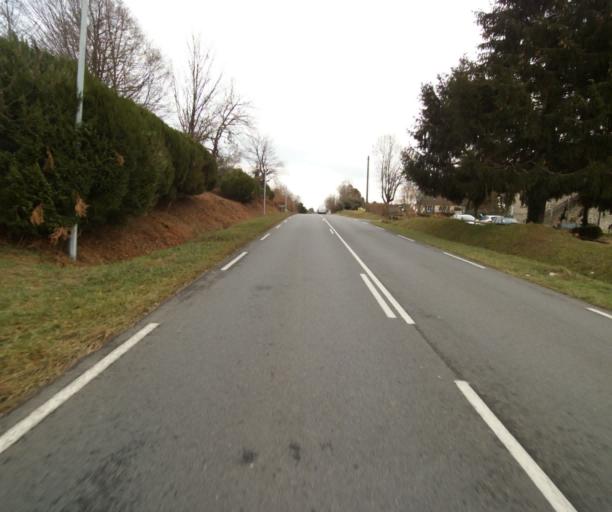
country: FR
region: Limousin
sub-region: Departement de la Correze
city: Chameyrat
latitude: 45.2675
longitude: 1.7076
